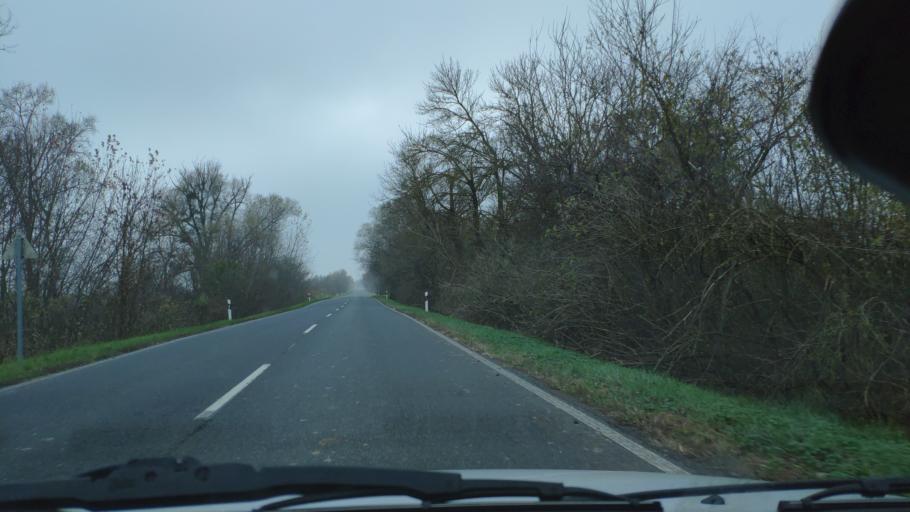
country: HU
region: Somogy
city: Balatonbereny
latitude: 46.6099
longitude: 17.2737
